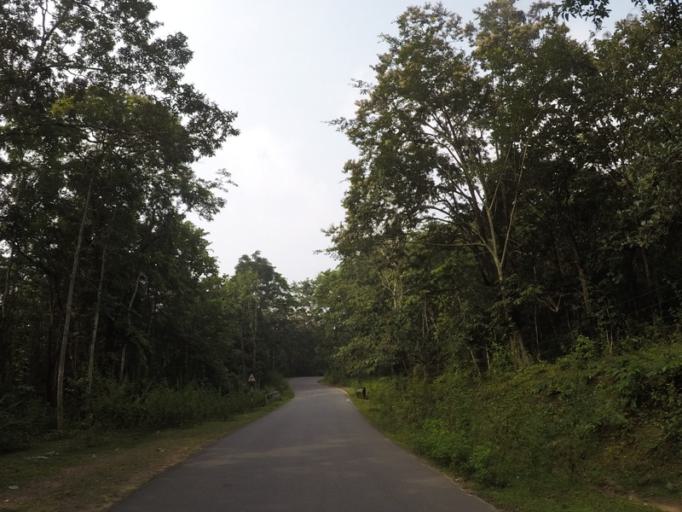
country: IN
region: Karnataka
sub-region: Chikmagalur
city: Koppa
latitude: 13.3588
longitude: 75.5008
